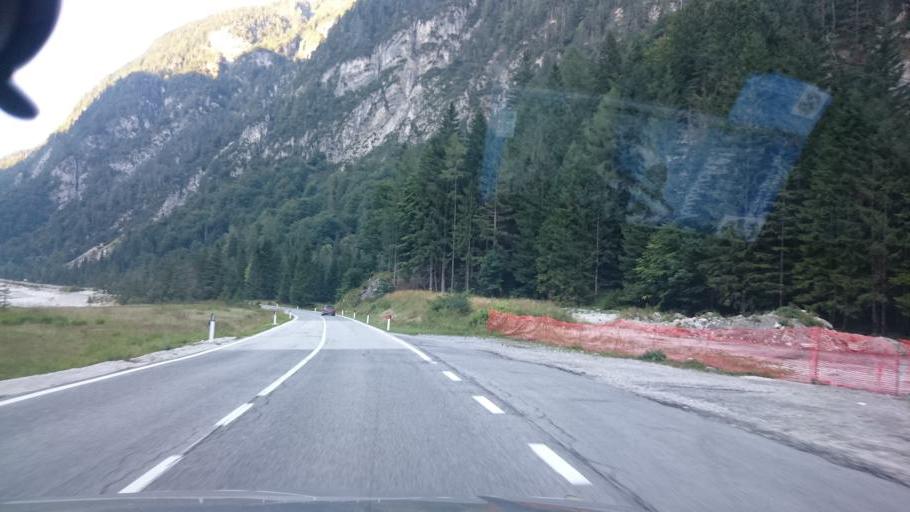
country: IT
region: Friuli Venezia Giulia
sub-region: Provincia di Udine
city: Tarvisio
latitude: 46.4488
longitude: 13.5741
